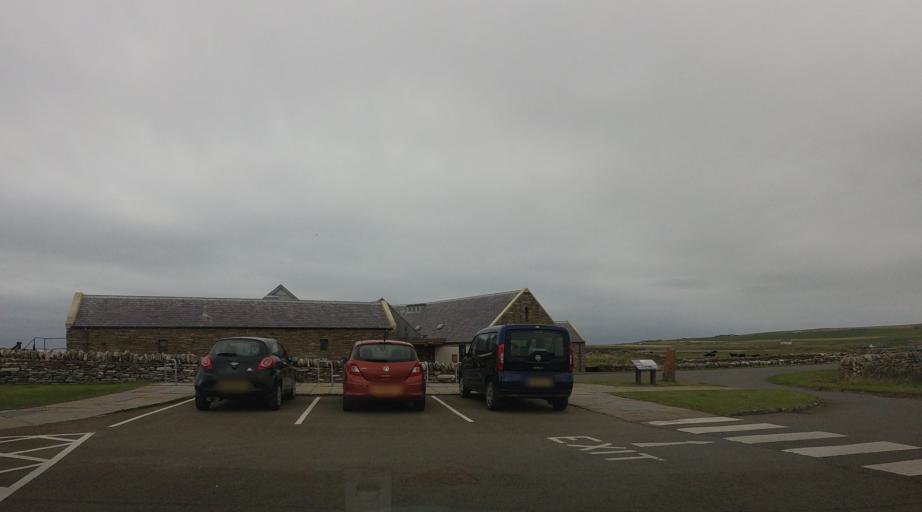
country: GB
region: Scotland
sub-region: Orkney Islands
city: Stromness
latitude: 59.0486
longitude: -3.3351
